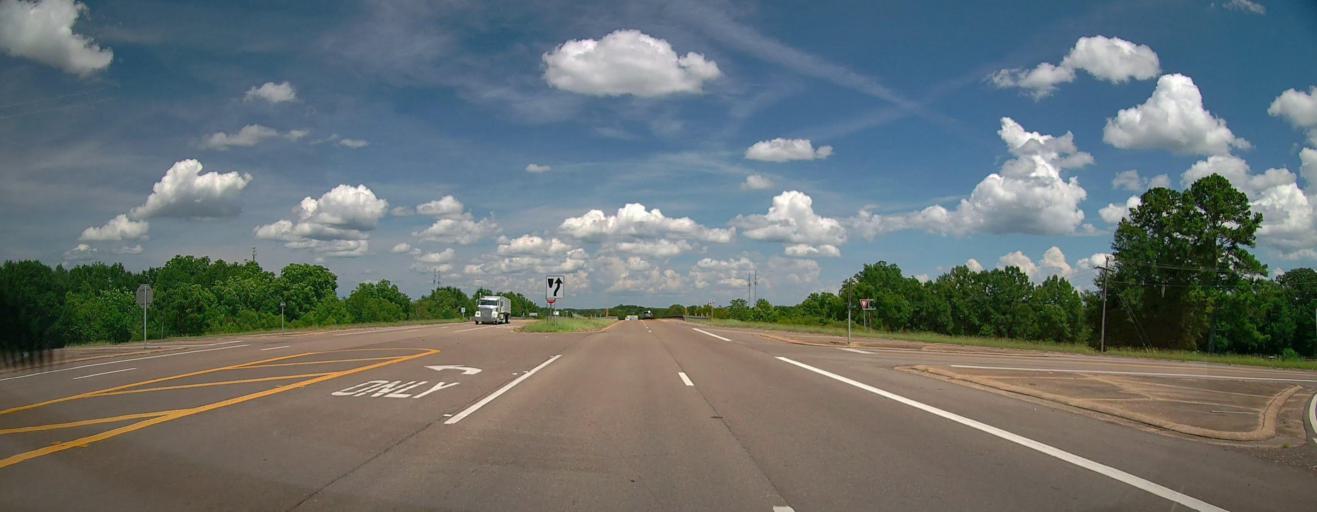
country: US
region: Mississippi
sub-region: Monroe County
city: Aberdeen
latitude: 33.8153
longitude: -88.5406
